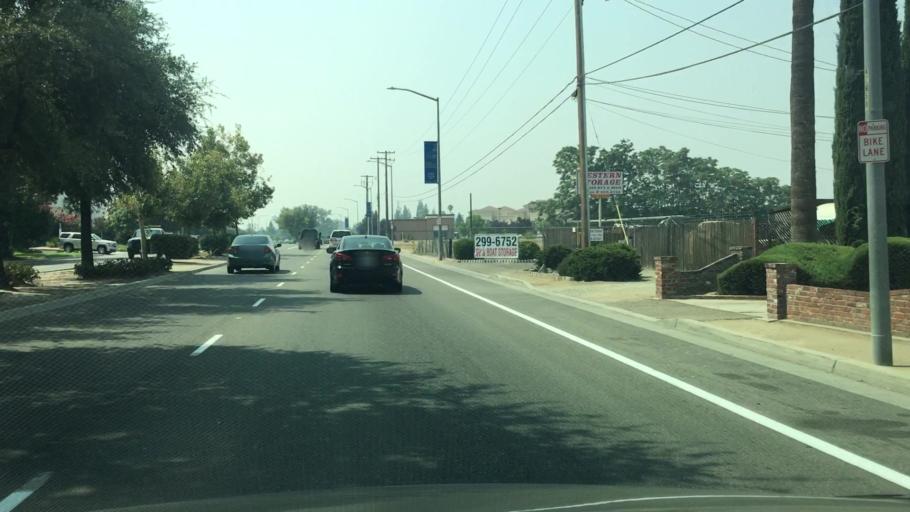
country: US
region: California
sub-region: Fresno County
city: Clovis
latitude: 36.8352
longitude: -119.7001
